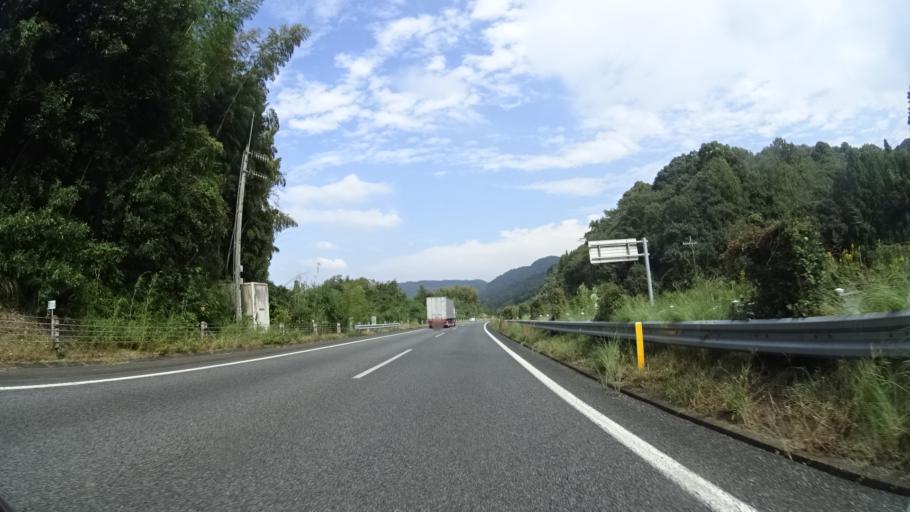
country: JP
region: Kumamoto
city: Matsubase
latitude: 32.5947
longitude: 130.7170
